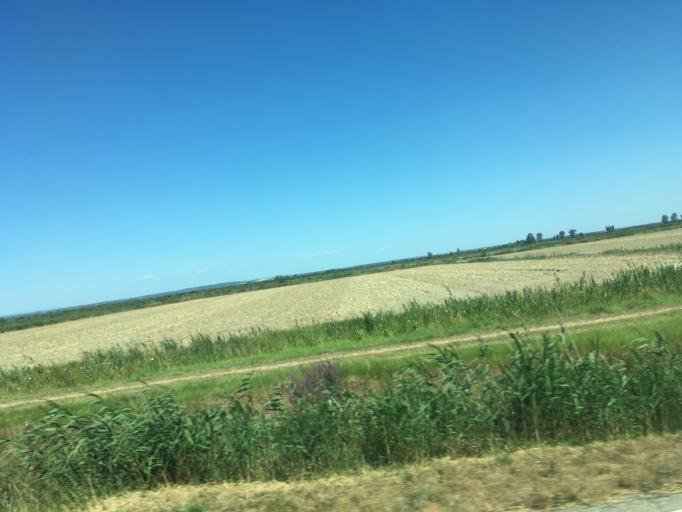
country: FR
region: Languedoc-Roussillon
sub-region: Departement du Gard
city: Fourques
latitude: 43.6342
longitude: 4.5463
